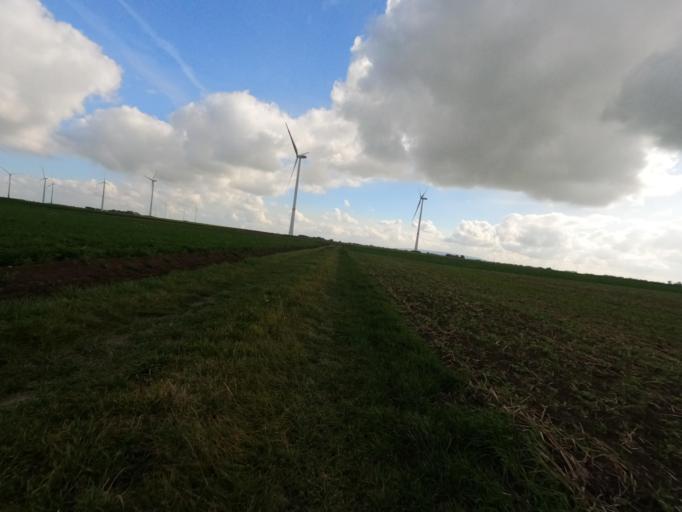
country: DE
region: North Rhine-Westphalia
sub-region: Regierungsbezirk Koln
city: Linnich
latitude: 51.0087
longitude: 6.2924
